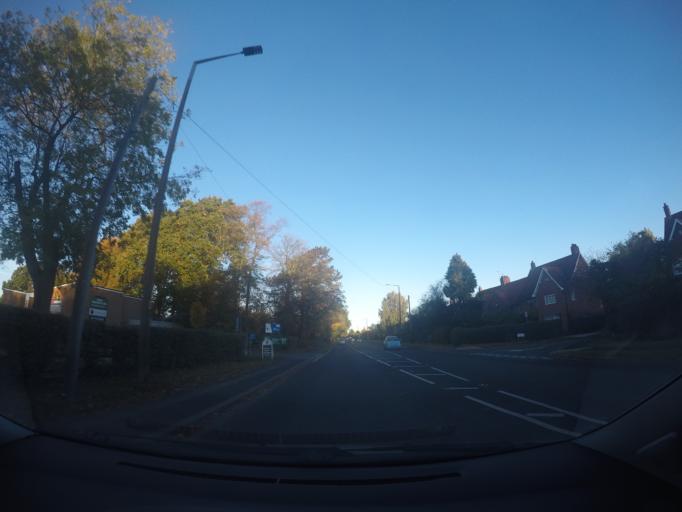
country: GB
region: England
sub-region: City of York
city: York
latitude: 53.9729
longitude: -1.1046
